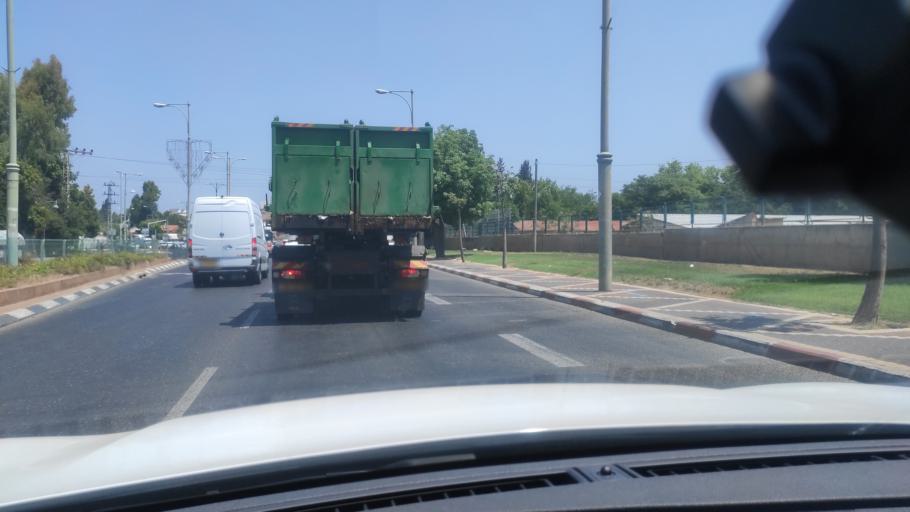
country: IL
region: Central District
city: Petah Tiqwa
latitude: 32.0956
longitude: 34.9019
